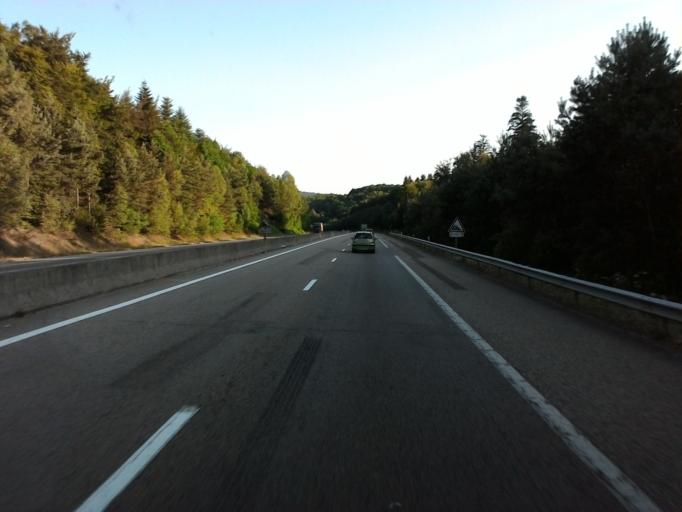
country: FR
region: Lorraine
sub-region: Departement des Vosges
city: Epinal
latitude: 48.1595
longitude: 6.4863
